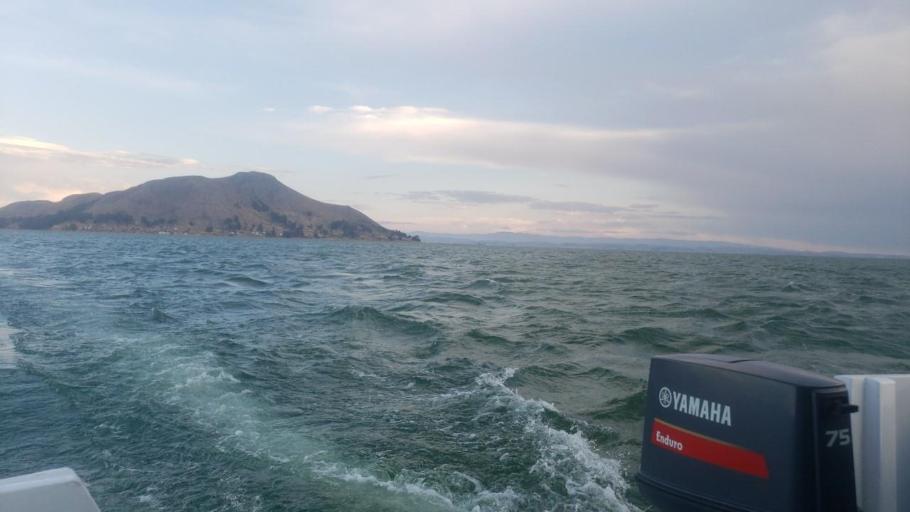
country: BO
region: La Paz
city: San Pedro
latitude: -16.2752
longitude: -68.7878
